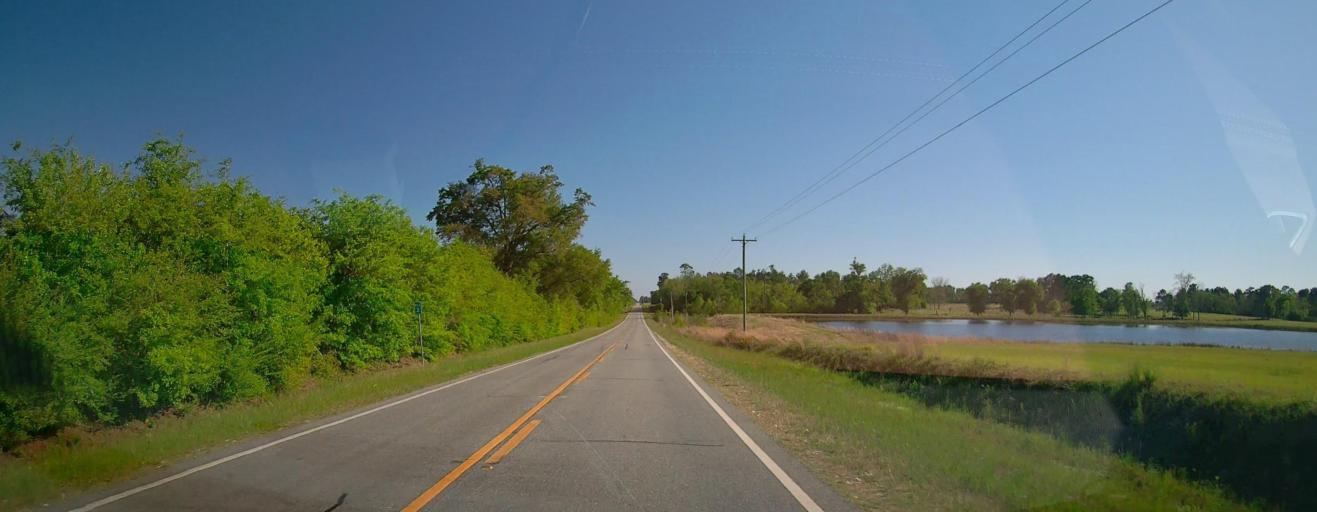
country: US
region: Georgia
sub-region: Wilcox County
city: Rochelle
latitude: 31.8762
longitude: -83.4888
